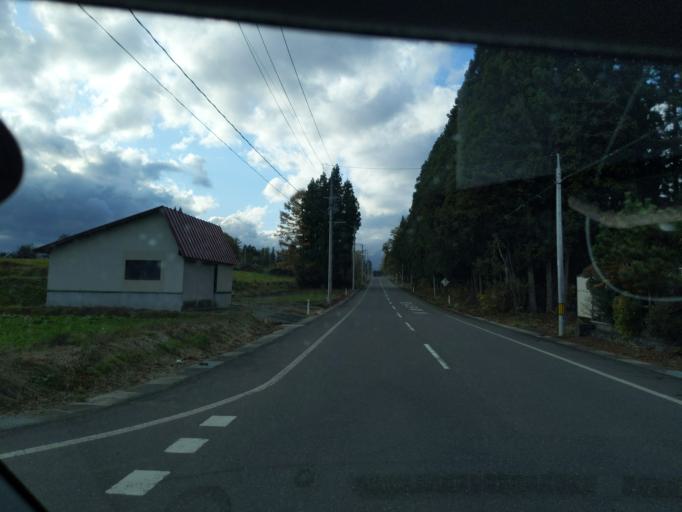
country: JP
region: Iwate
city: Mizusawa
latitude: 39.1097
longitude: 141.0010
